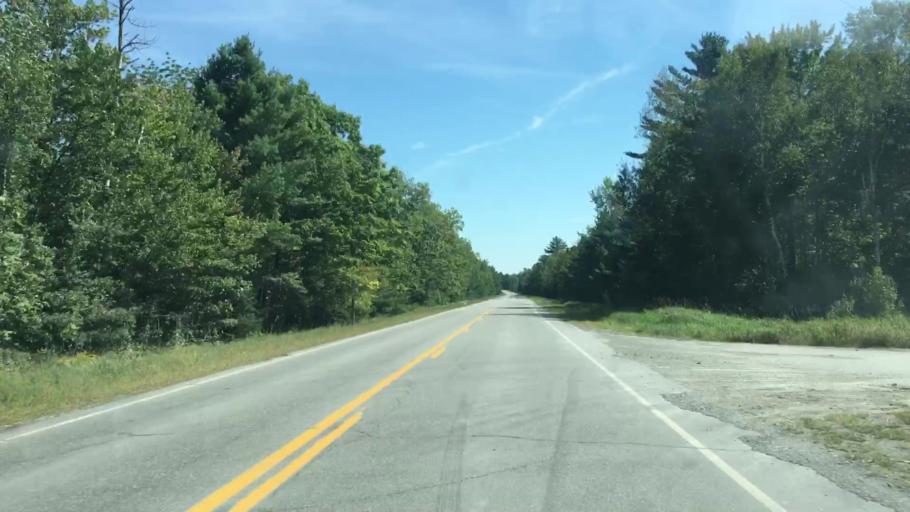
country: US
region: Maine
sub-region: Piscataquis County
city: Milo
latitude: 45.2265
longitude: -68.9305
